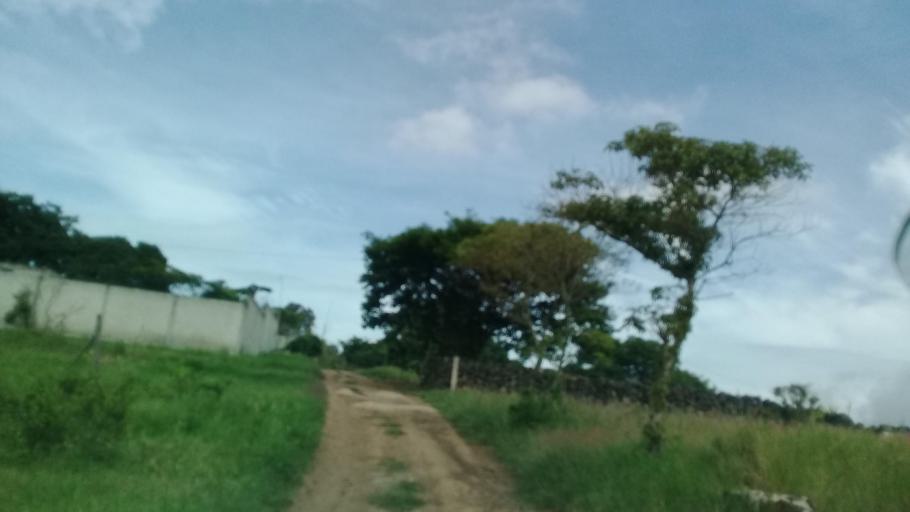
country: MX
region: Veracruz
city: El Castillo
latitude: 19.5547
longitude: -96.8791
